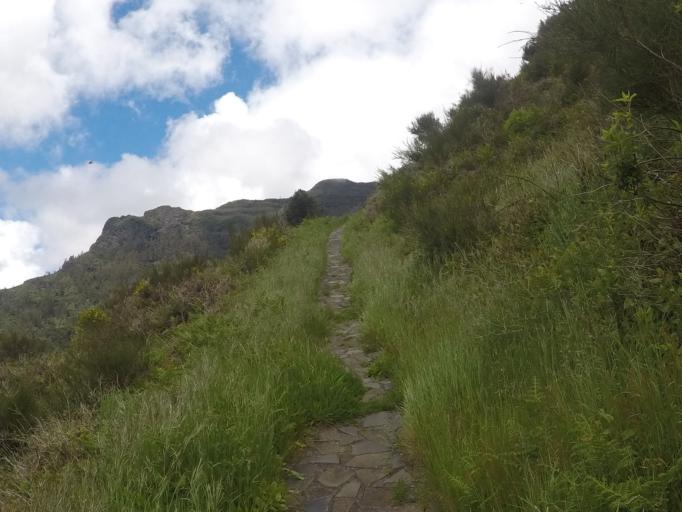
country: PT
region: Madeira
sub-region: Camara de Lobos
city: Curral das Freiras
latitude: 32.7401
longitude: -17.0058
